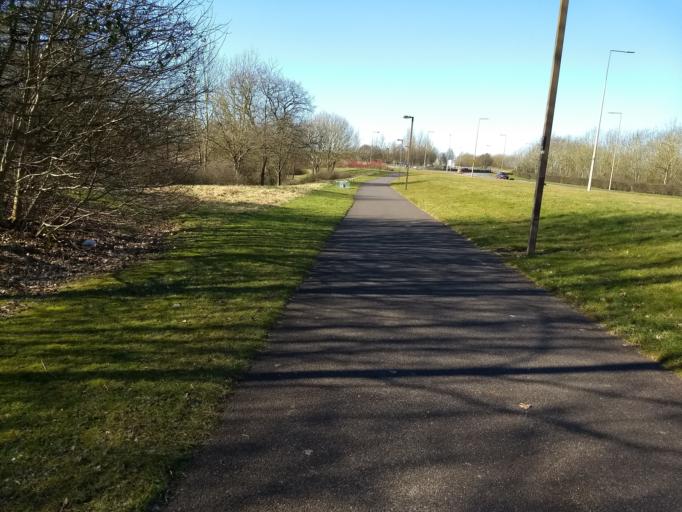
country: GB
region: England
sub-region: Milton Keynes
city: Shenley Church End
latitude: 52.0034
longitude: -0.7870
